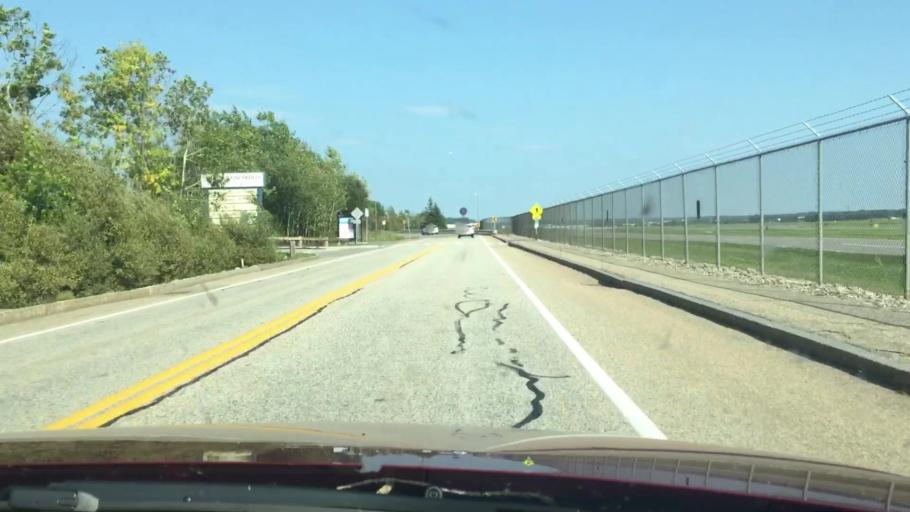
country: US
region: Maine
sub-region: Cumberland County
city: South Portland Gardens
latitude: 43.6473
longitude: -70.3200
